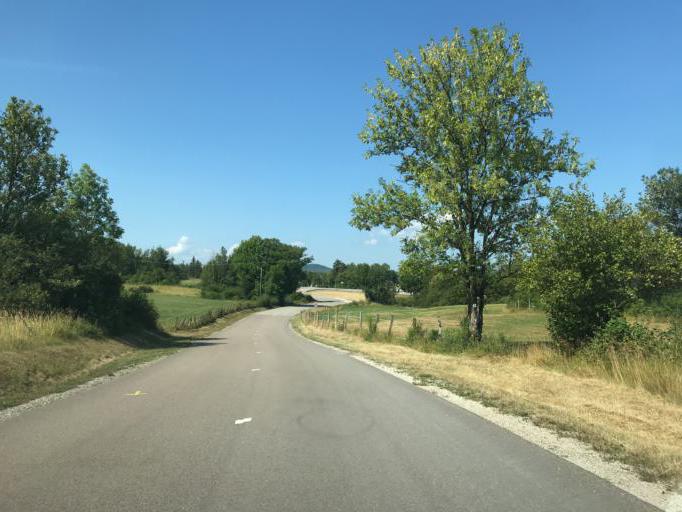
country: FR
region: Franche-Comte
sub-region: Departement du Jura
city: Moirans-en-Montagne
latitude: 46.4672
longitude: 5.7188
